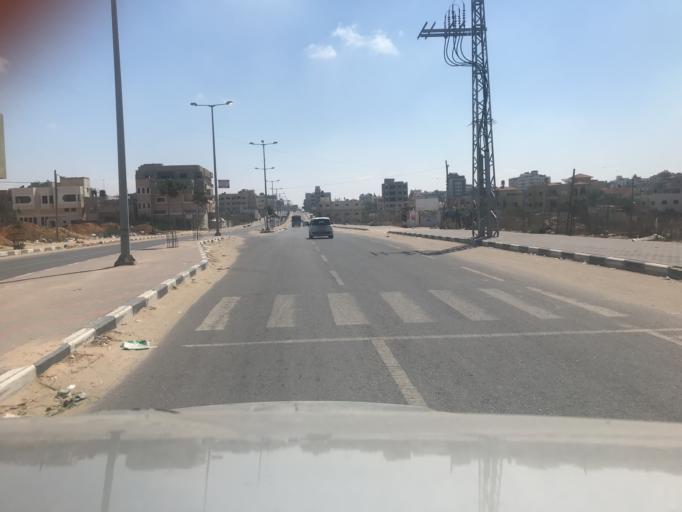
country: PS
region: Gaza Strip
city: Bayt Lahya
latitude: 31.5529
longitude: 34.4689
